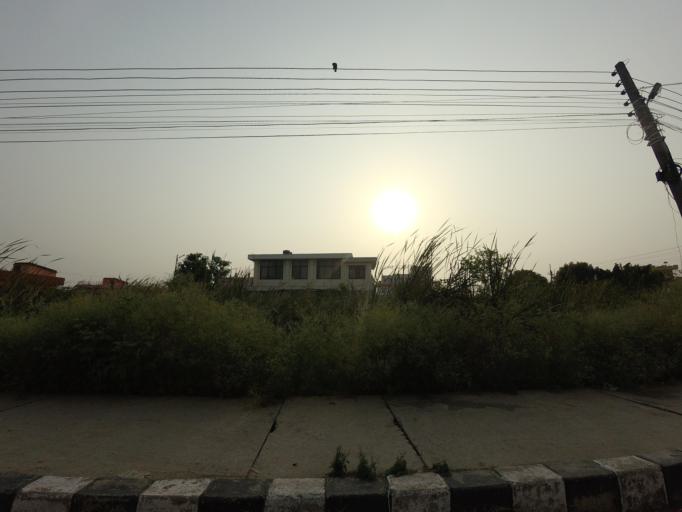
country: NP
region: Western Region
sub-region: Lumbini Zone
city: Bhairahawa
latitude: 27.5109
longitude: 83.4609
